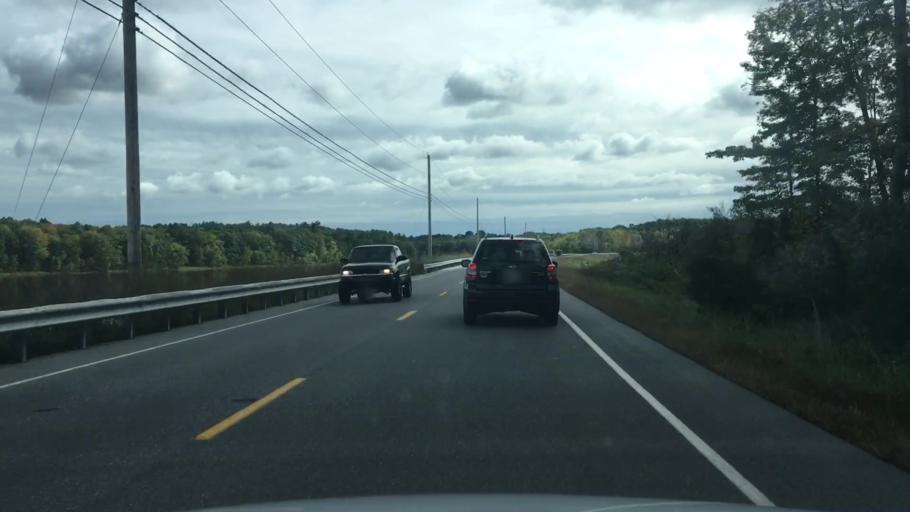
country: US
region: Maine
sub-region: Androscoggin County
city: Lisbon
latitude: 43.9932
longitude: -70.1415
